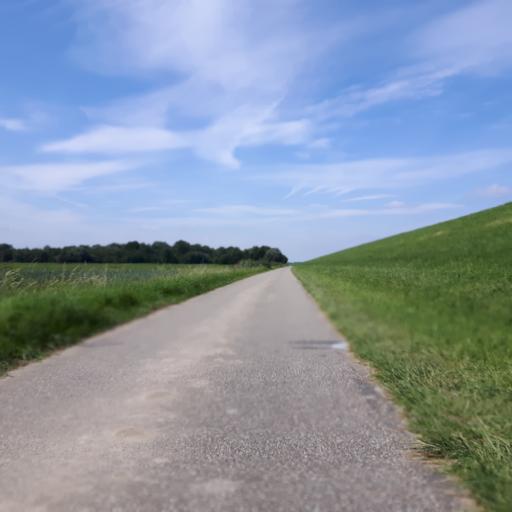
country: NL
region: Zeeland
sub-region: Schouwen-Duiveland
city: Bruinisse
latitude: 51.6484
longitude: 4.1461
